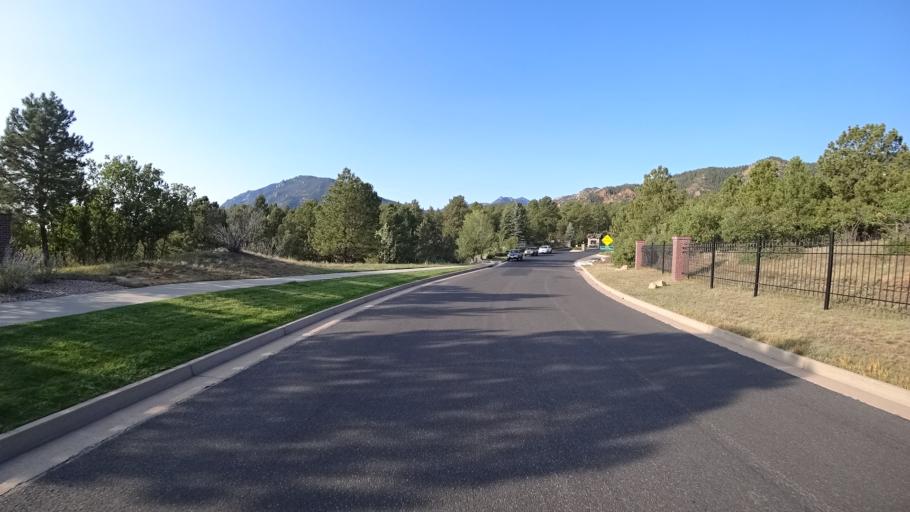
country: US
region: Colorado
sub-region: El Paso County
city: Colorado Springs
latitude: 38.8048
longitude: -104.8620
